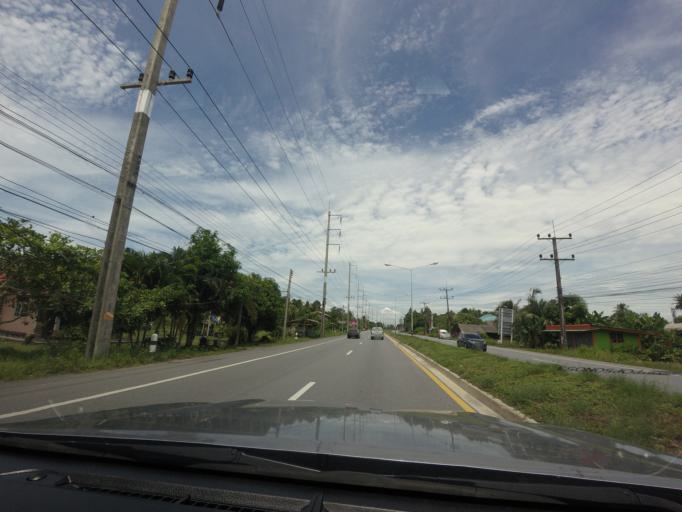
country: TH
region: Songkhla
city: Krasae Sin
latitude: 7.5947
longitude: 100.4036
